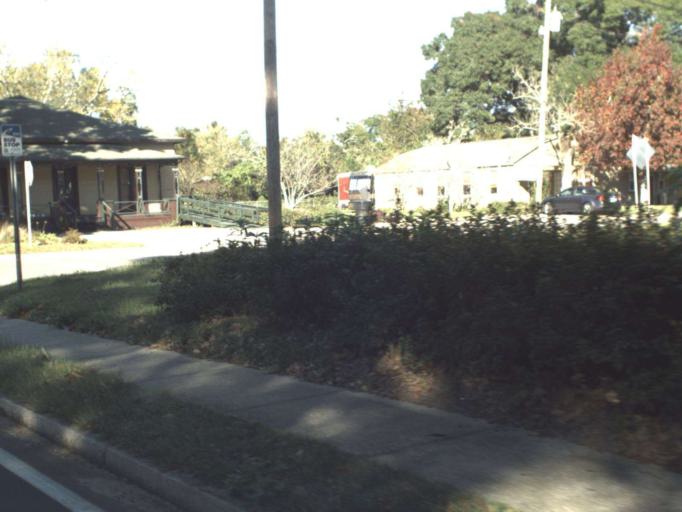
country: US
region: Florida
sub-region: Escambia County
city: Goulding
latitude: 30.4389
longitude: -87.2106
